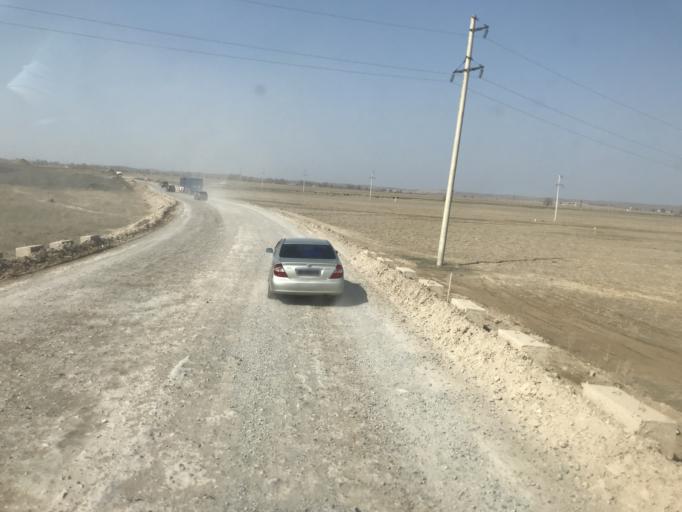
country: KG
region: Chuy
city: Bystrovka
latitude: 43.3227
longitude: 76.0408
